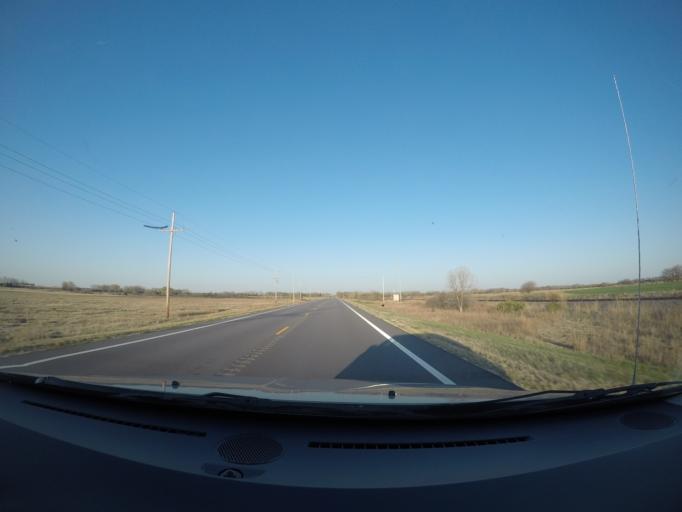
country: US
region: Kansas
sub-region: Stafford County
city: Stafford
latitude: 37.8354
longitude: -98.3694
